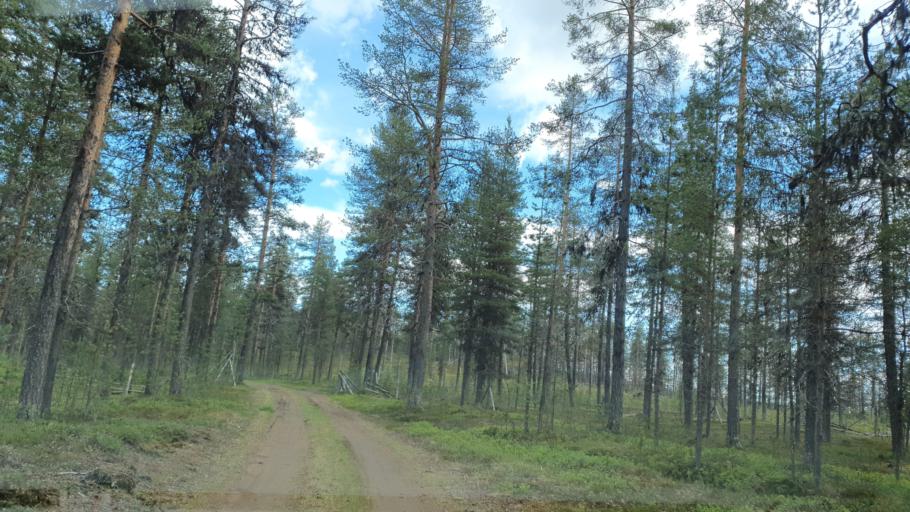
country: FI
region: Lapland
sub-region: Tunturi-Lappi
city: Kolari
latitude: 67.5370
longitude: 23.9151
